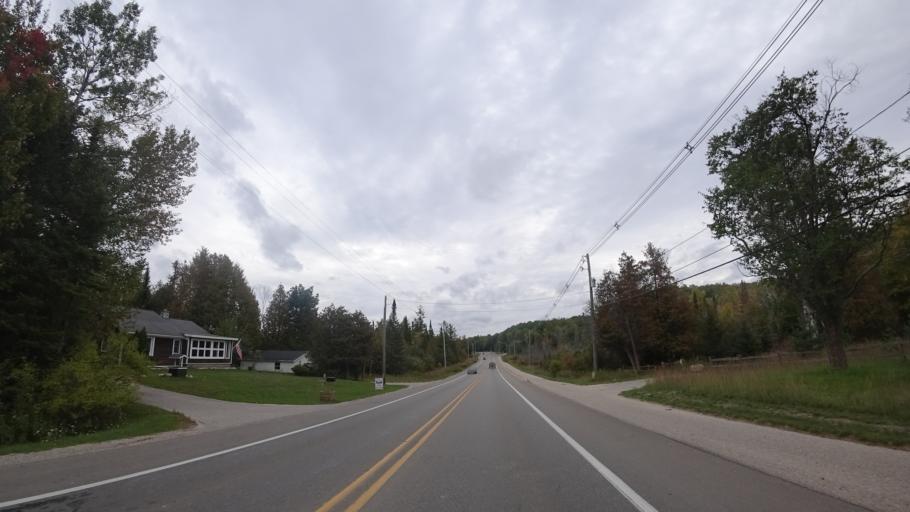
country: US
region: Michigan
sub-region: Emmet County
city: Petoskey
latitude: 45.4178
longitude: -84.9045
